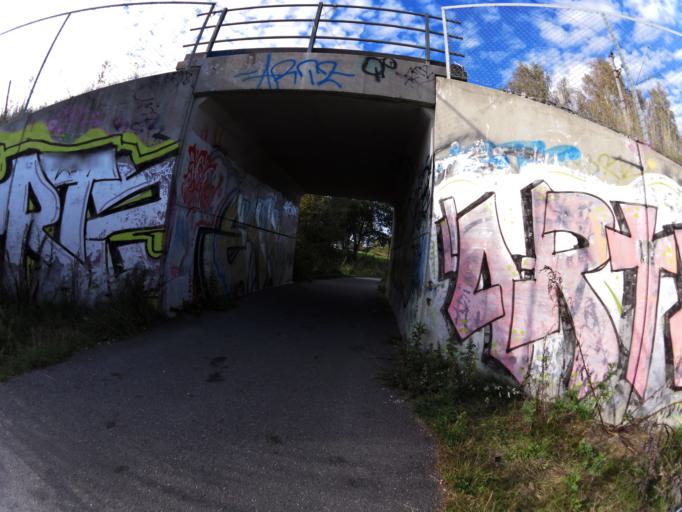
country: NO
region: Ostfold
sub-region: Sarpsborg
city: Sarpsborg
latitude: 59.2858
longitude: 11.0946
